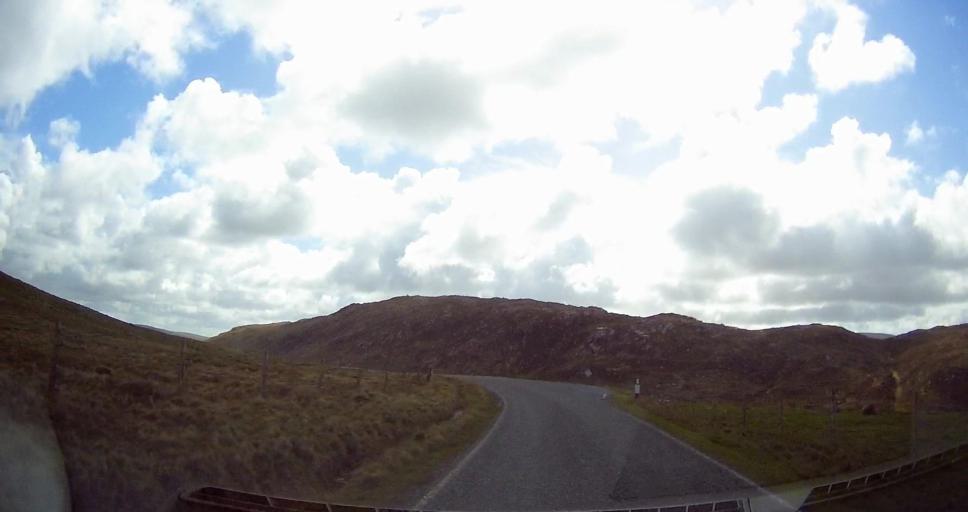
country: GB
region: Scotland
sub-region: Shetland Islands
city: Lerwick
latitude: 60.5575
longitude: -1.3376
